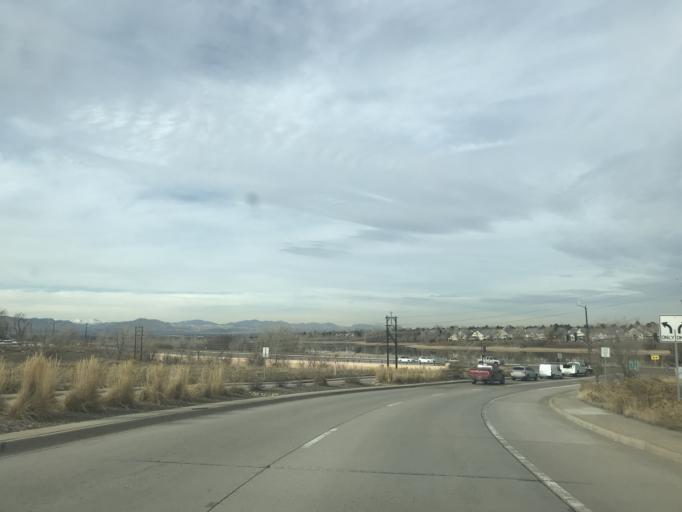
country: US
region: Colorado
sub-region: Douglas County
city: Highlands Ranch
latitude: 39.5640
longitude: -105.0100
